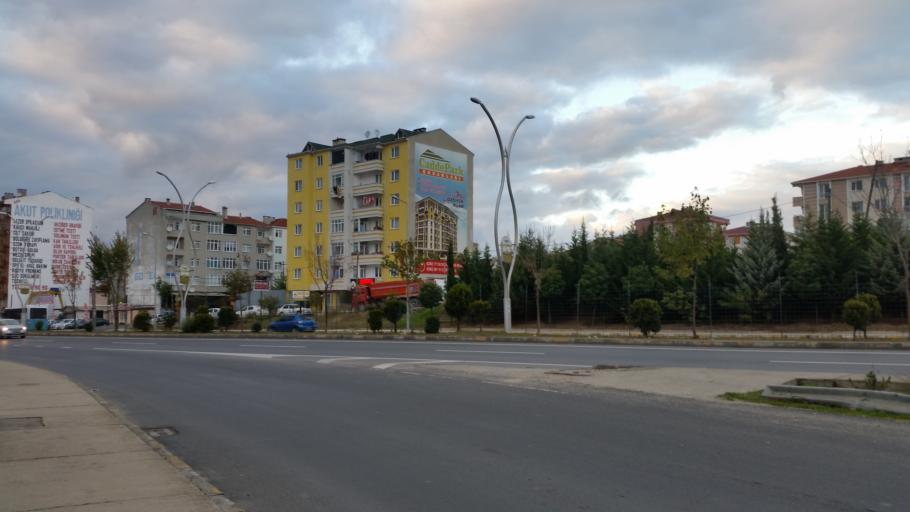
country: TR
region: Tekirdag
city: Cerkezkoey
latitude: 41.3198
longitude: 27.9826
